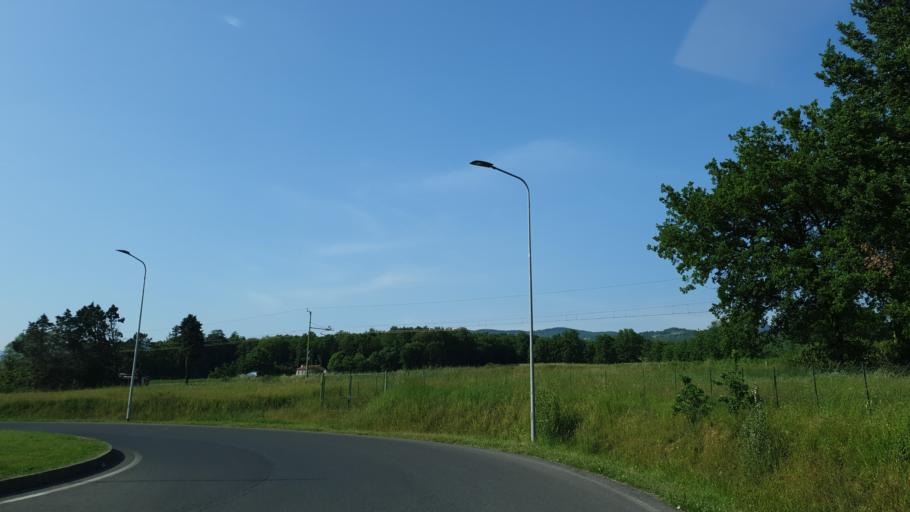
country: IT
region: Tuscany
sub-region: Province of Arezzo
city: Ponte a Poppi
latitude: 43.7379
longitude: 11.7531
